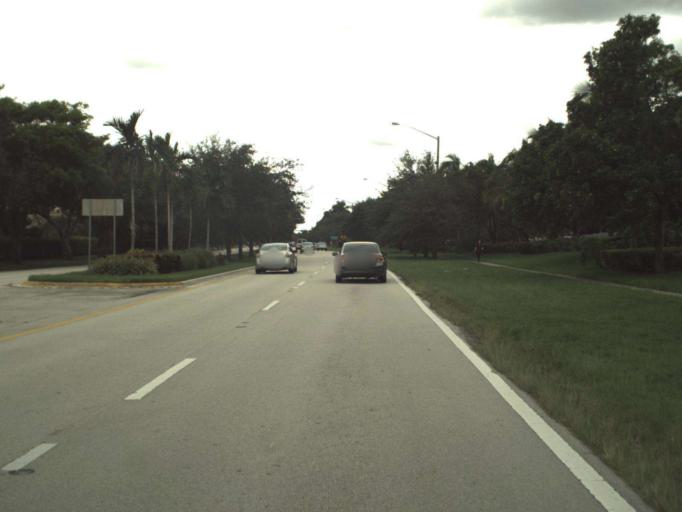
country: US
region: Florida
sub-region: Broward County
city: Coral Springs
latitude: 26.2385
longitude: -80.2808
